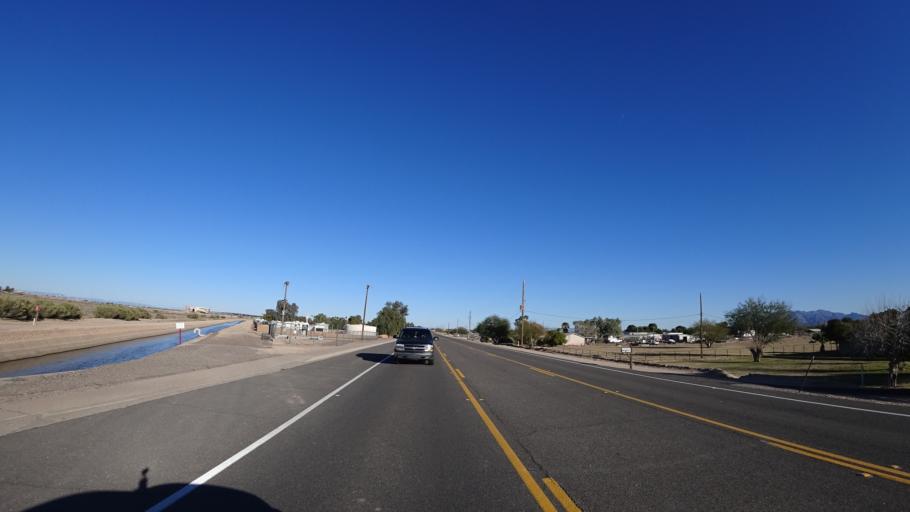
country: US
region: Arizona
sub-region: Maricopa County
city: Goodyear
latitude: 33.4502
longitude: -112.4516
